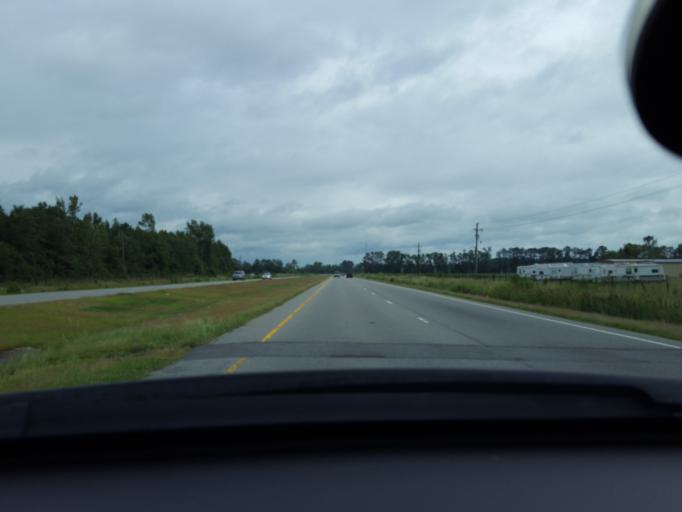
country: US
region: North Carolina
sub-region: Pitt County
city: Ayden
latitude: 35.4607
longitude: -77.4341
